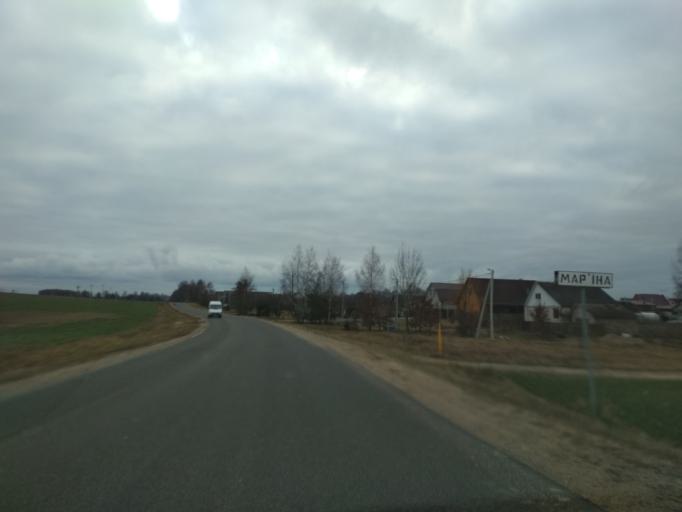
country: BY
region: Minsk
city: Mar''ina Horka
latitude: 53.5425
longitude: 28.1308
